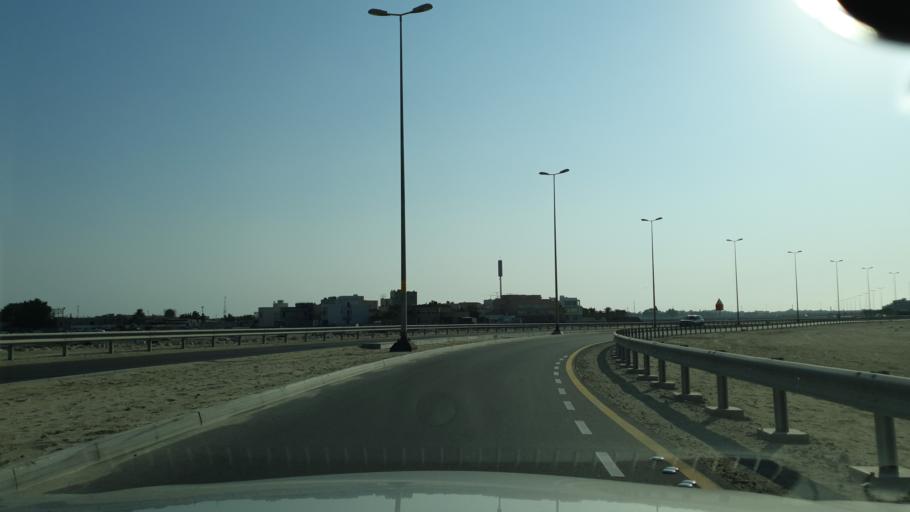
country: BH
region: Manama
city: Jidd Hafs
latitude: 26.2324
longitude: 50.4621
